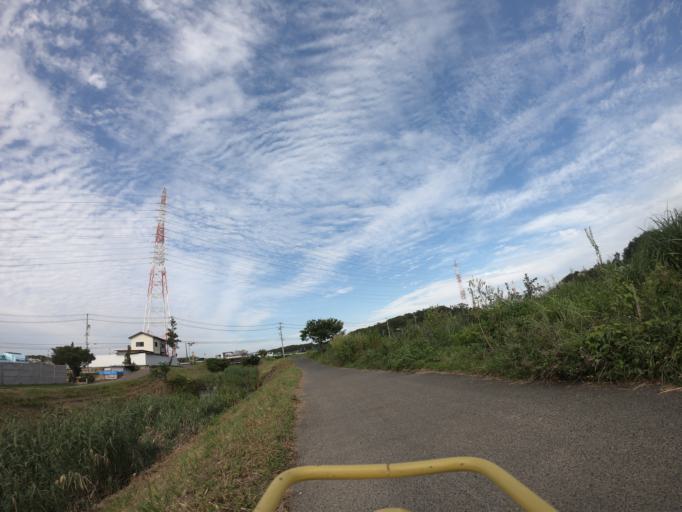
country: JP
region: Aichi
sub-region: Toyota-shi
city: Toyota
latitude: 35.1317
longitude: 137.0710
